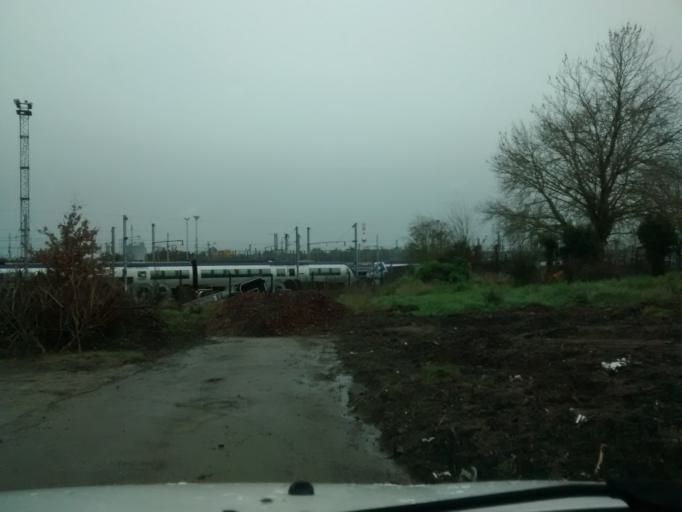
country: FR
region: Brittany
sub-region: Departement d'Ille-et-Vilaine
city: Chantepie
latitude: 48.1061
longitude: -1.6330
